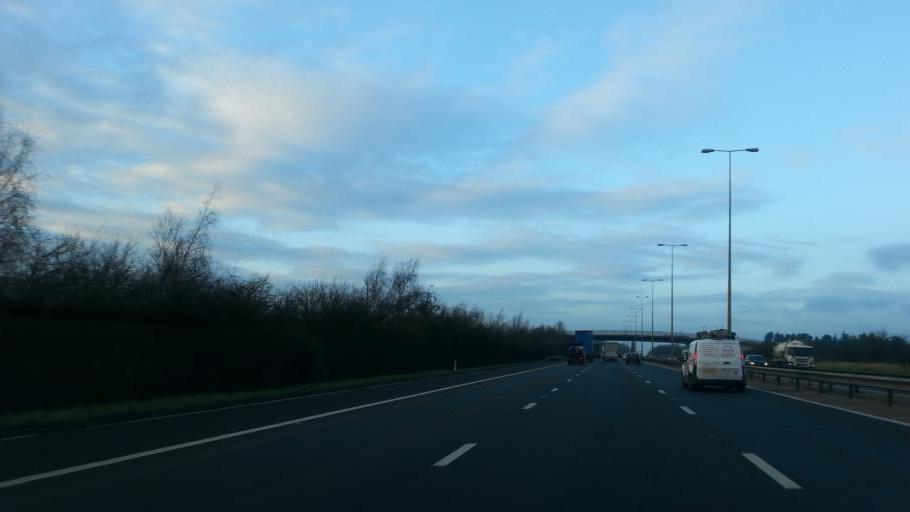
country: GB
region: England
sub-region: Worcestershire
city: Upton upon Severn
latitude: 52.0899
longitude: -2.1807
